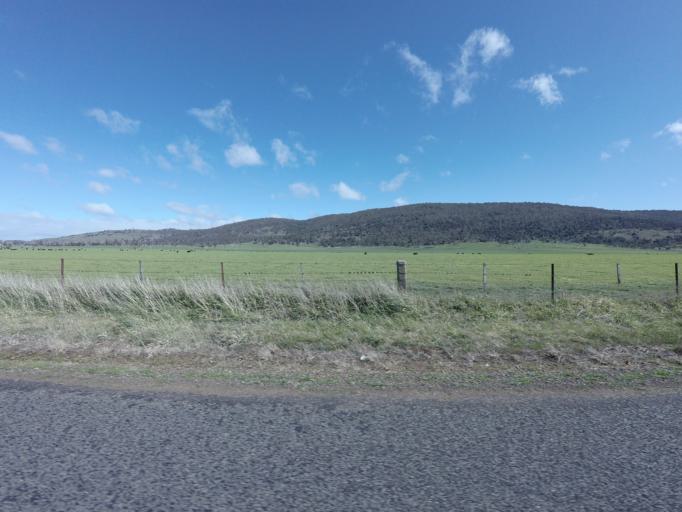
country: AU
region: Tasmania
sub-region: Northern Midlands
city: Evandale
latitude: -41.9768
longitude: 147.4464
